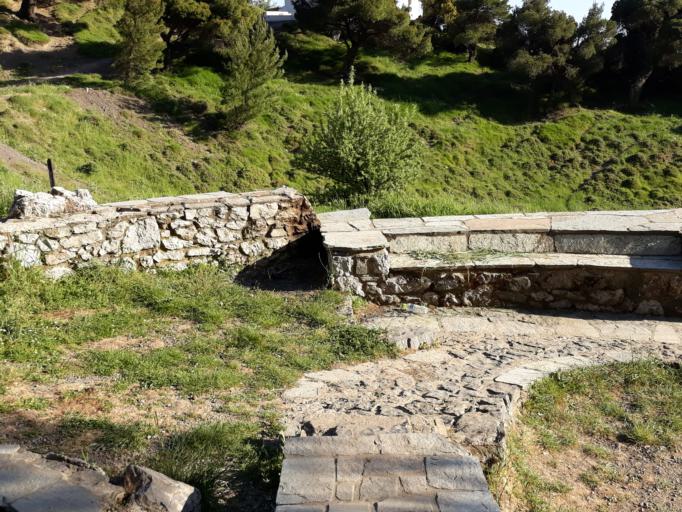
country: GR
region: Attica
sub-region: Nomarchia Dytikis Attikis
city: Fyli
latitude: 38.1467
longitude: 23.6465
